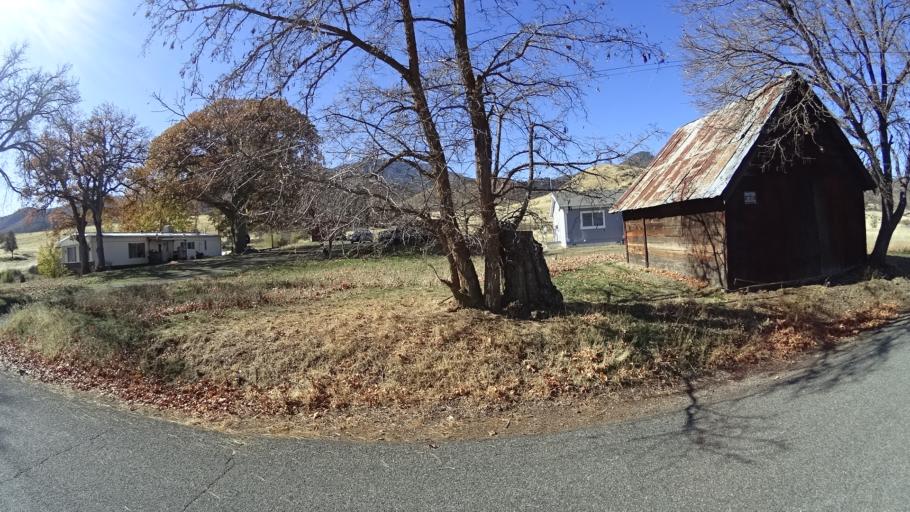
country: US
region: California
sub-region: Siskiyou County
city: Yreka
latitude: 41.9238
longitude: -122.5790
